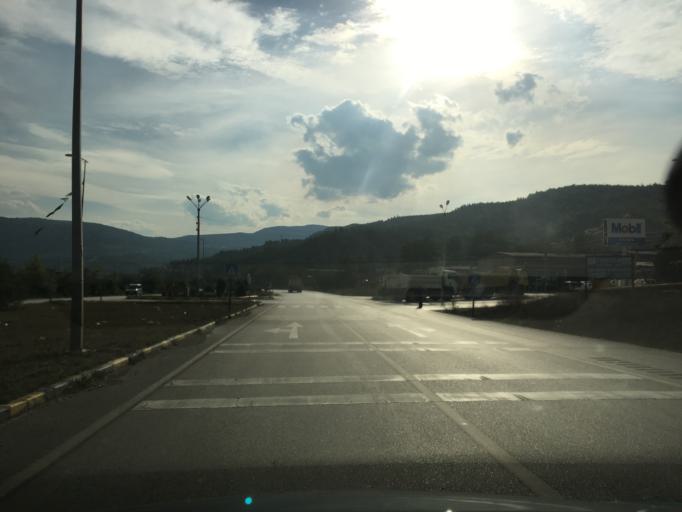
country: TR
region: Karabuk
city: Karabuk
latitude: 41.1198
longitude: 32.6753
